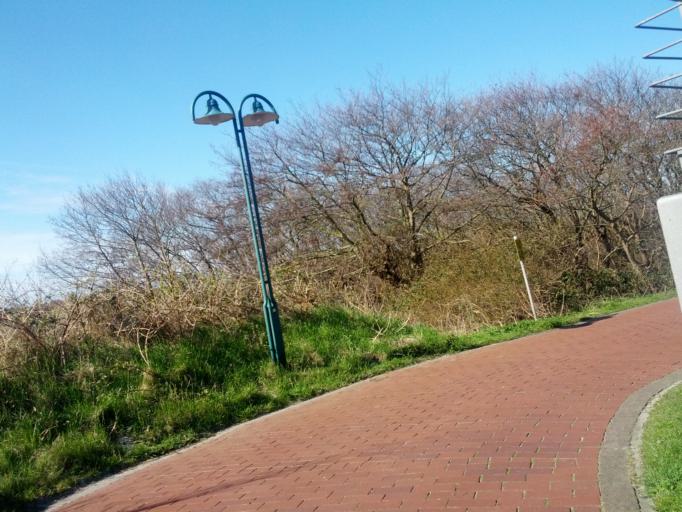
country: DE
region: Lower Saxony
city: Langeoog
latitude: 53.7497
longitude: 7.4791
